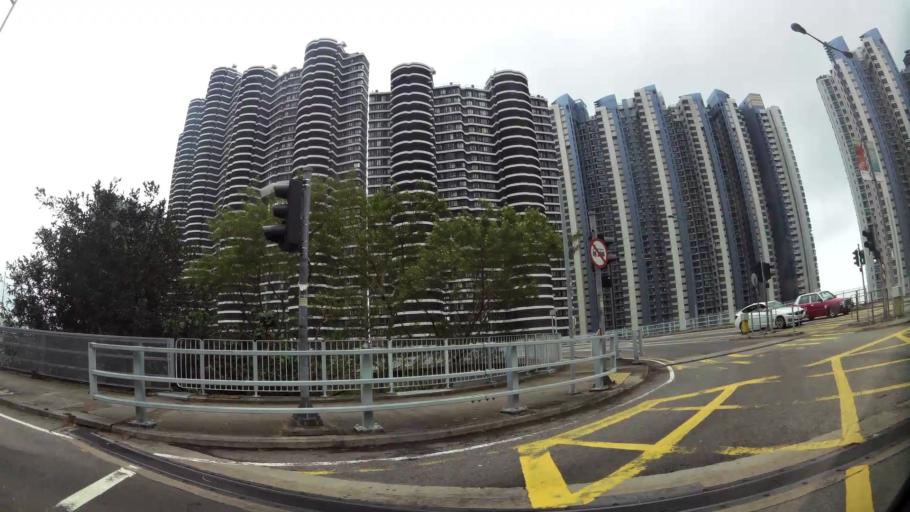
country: HK
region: Central and Western
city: Central
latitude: 22.2566
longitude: 114.1341
